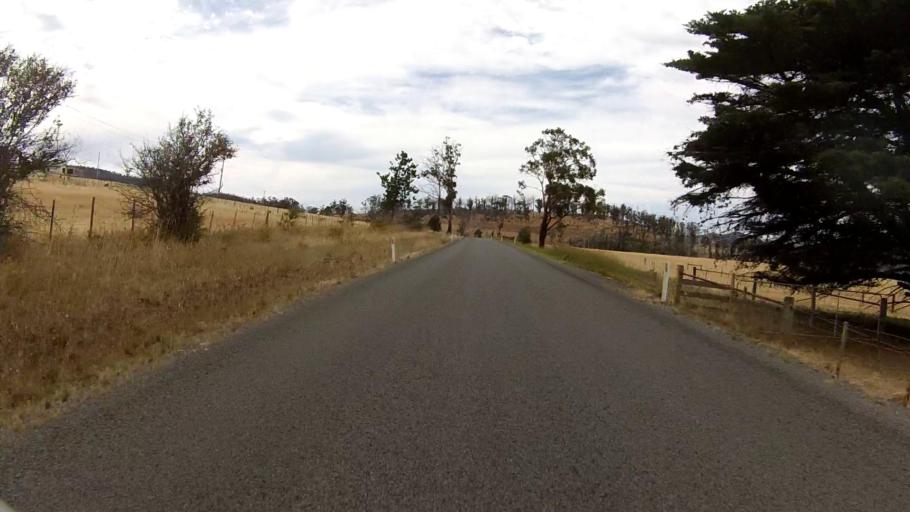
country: AU
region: Tasmania
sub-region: Sorell
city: Sorell
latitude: -42.8963
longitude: 147.7723
